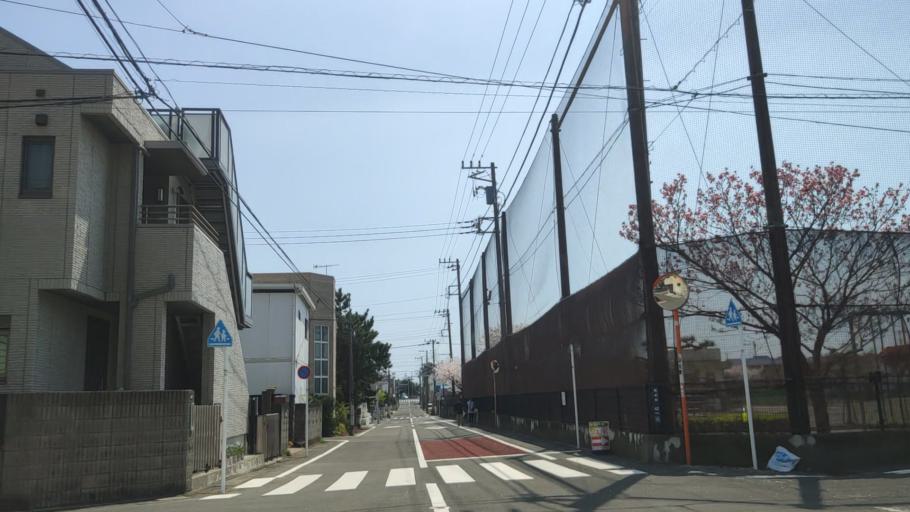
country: JP
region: Kanagawa
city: Hiratsuka
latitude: 35.3176
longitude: 139.3395
